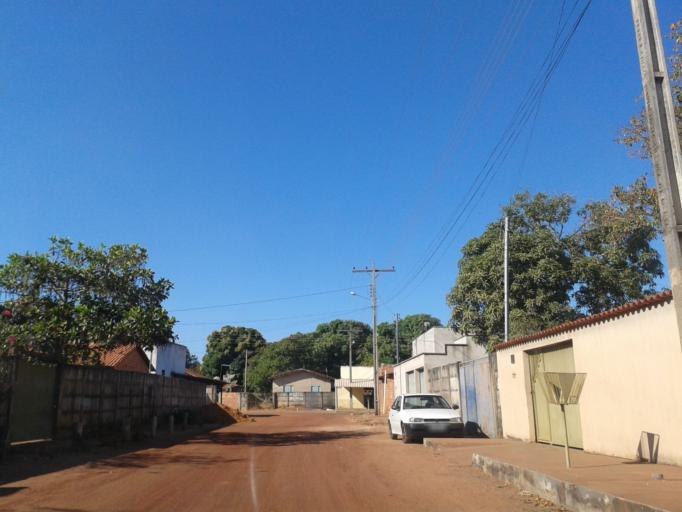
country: BR
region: Goias
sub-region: Sao Miguel Do Araguaia
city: Sao Miguel do Araguaia
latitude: -13.2845
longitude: -50.1769
